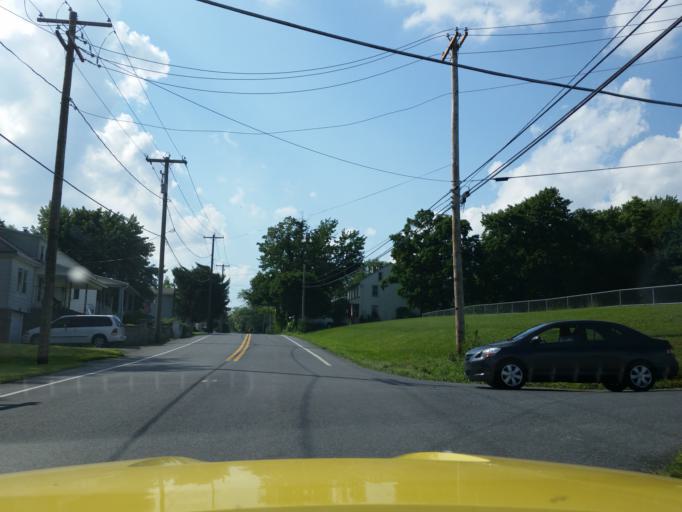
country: US
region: Pennsylvania
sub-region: Lancaster County
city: Mount Joy
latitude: 40.1956
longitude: -76.4855
